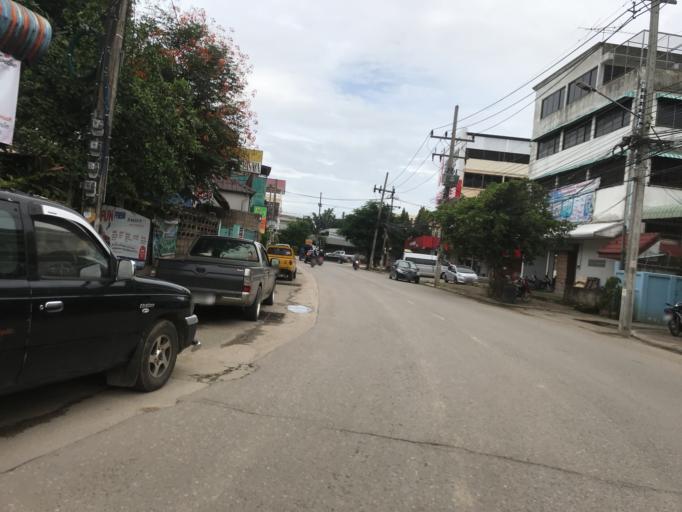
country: TH
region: Chiang Rai
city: Chiang Rai
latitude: 19.8977
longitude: 99.8312
